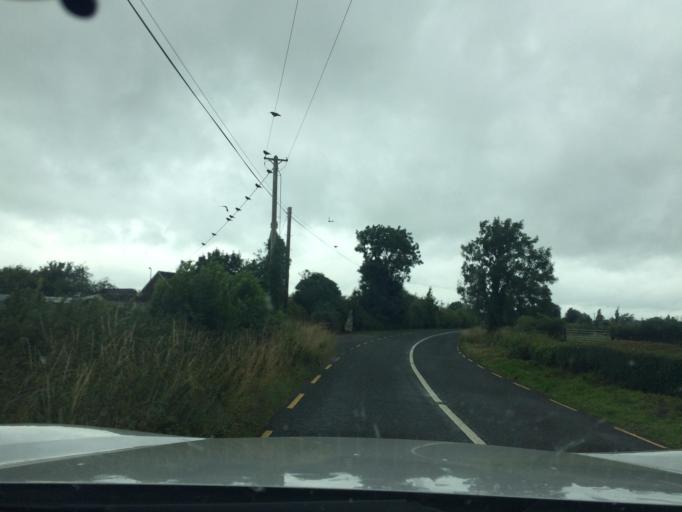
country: IE
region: Munster
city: Cashel
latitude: 52.6159
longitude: -7.8805
